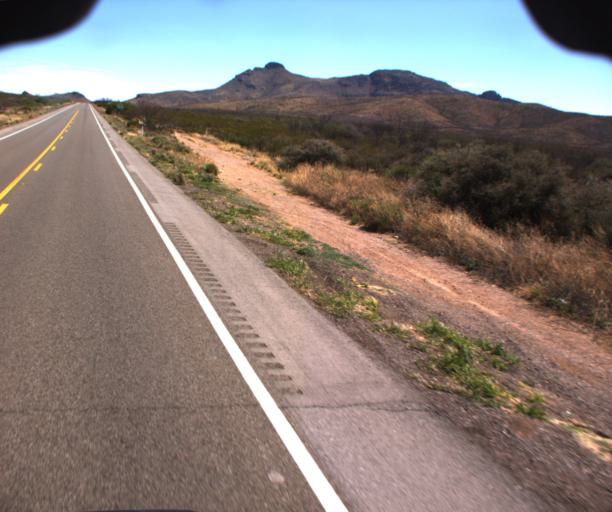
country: US
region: Arizona
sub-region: Cochise County
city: Douglas
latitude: 31.4426
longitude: -109.4748
